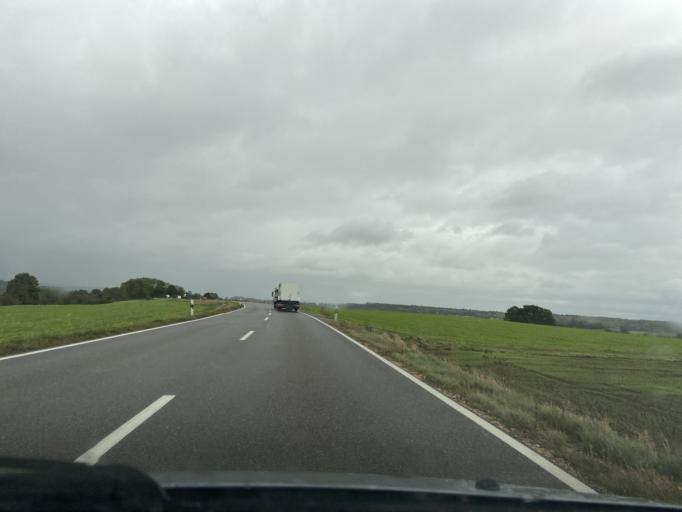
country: DE
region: Baden-Wuerttemberg
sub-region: Tuebingen Region
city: Krauchenwies
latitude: 48.0236
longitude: 9.2745
